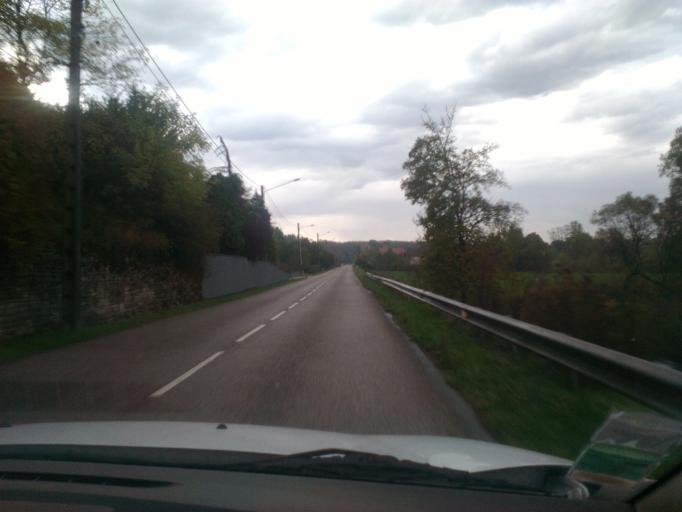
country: FR
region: Lorraine
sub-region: Departement des Vosges
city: Chatel-sur-Moselle
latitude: 48.3031
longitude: 6.4109
